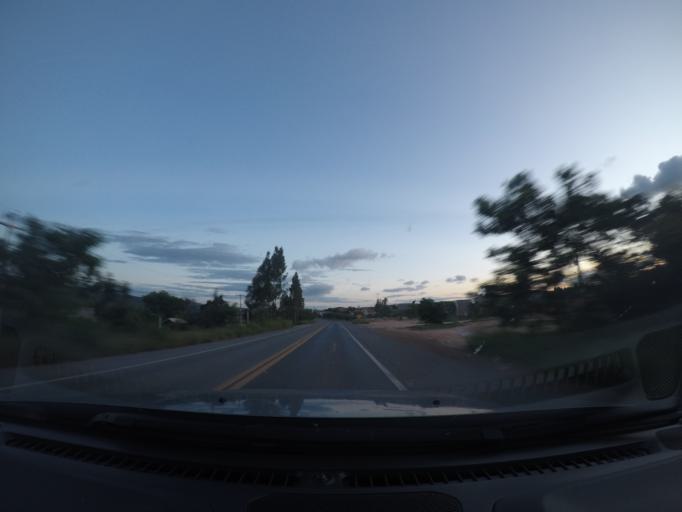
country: BR
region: Bahia
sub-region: Seabra
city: Seabra
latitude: -12.4567
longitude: -41.7496
